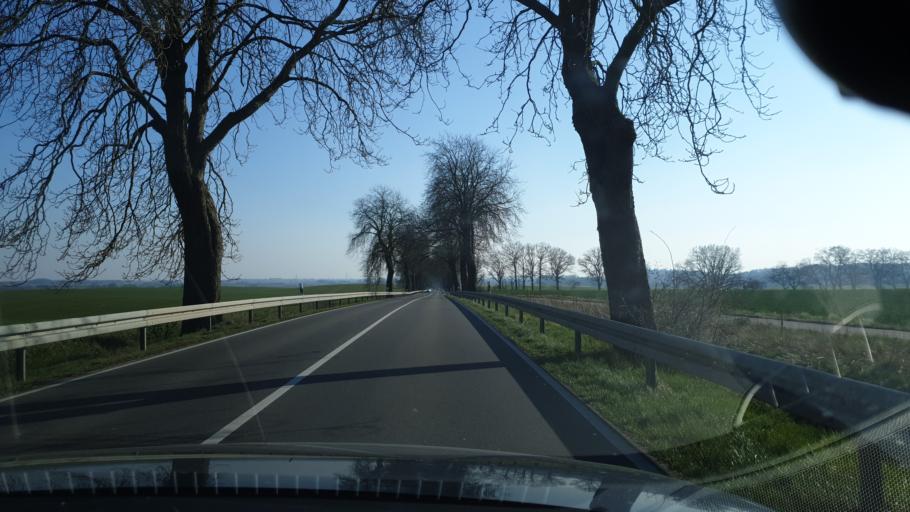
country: DE
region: Mecklenburg-Vorpommern
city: Lubstorf
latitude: 53.7104
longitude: 11.3984
